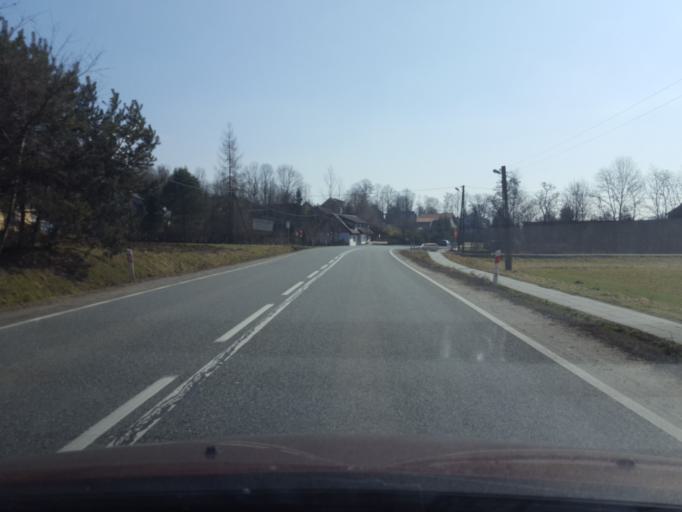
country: PL
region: Lesser Poland Voivodeship
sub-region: Powiat brzeski
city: Czchow
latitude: 49.8533
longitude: 20.6658
